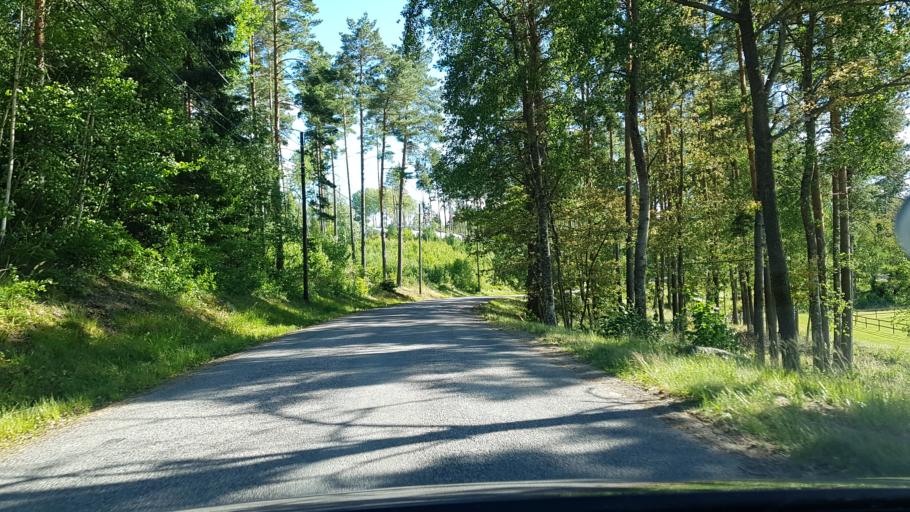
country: SE
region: Stockholm
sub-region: Upplands-Bro Kommun
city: Kungsaengen
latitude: 59.4860
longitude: 17.8032
